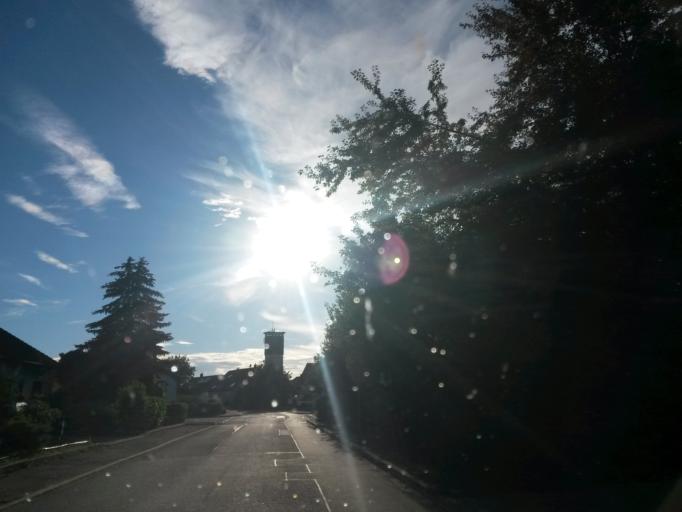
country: DE
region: Baden-Wuerttemberg
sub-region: Regierungsbezirk Stuttgart
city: Ellenberg
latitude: 49.0156
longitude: 10.2181
